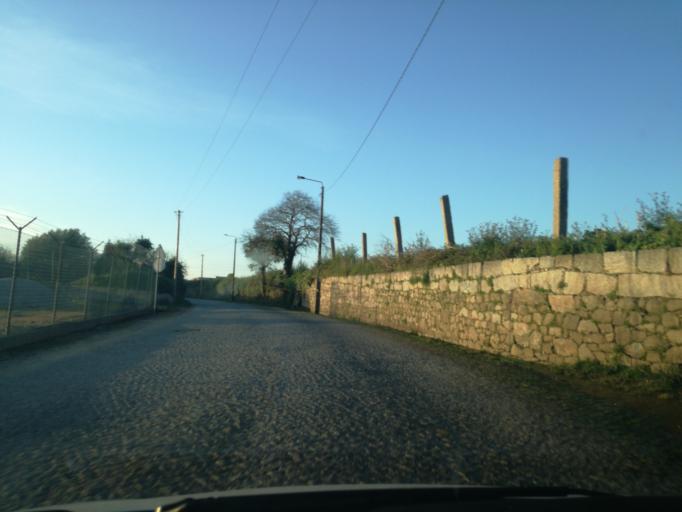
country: PT
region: Porto
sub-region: Matosinhos
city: Santa Cruz do Bispo
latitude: 41.2592
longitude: -8.6798
